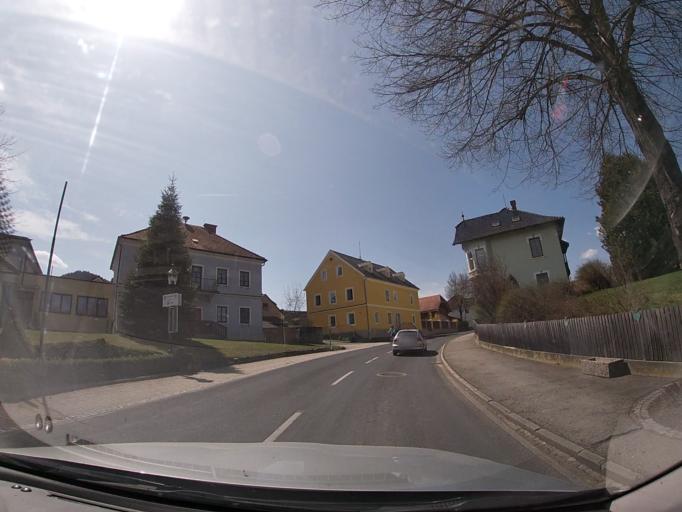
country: AT
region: Styria
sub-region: Politischer Bezirk Murtal
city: Sankt Lorenzen bei Knittelfeld
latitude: 47.2499
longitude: 14.8954
